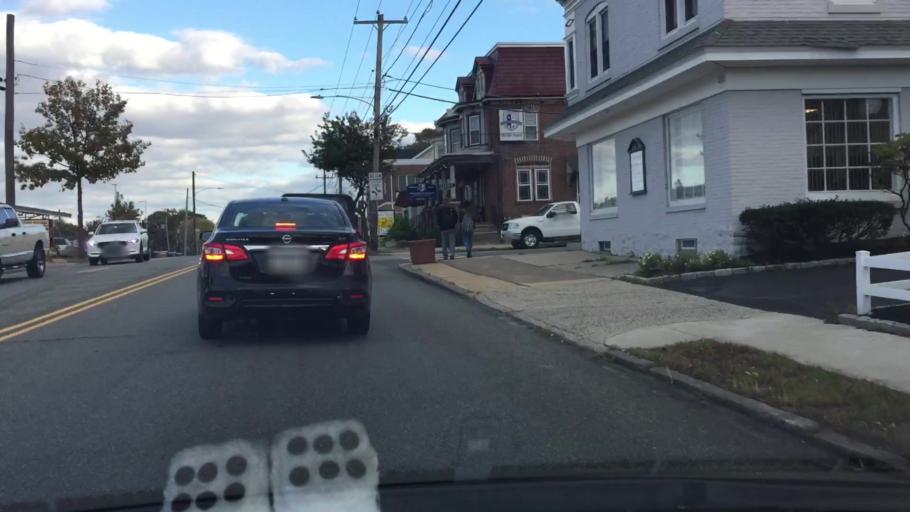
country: US
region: Pennsylvania
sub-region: Delaware County
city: Media
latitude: 39.9158
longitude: -75.3827
